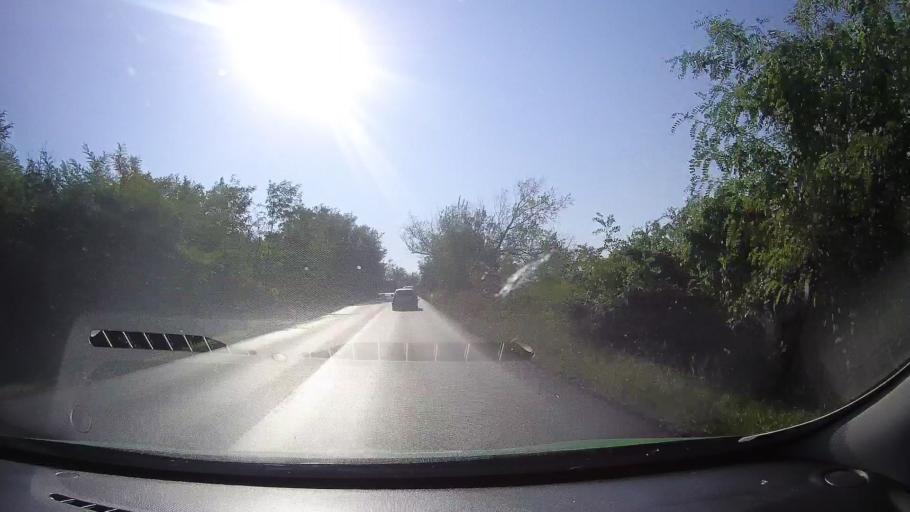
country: RO
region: Timis
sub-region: Comuna Curtea
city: Curtea
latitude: 45.8485
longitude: 22.3212
